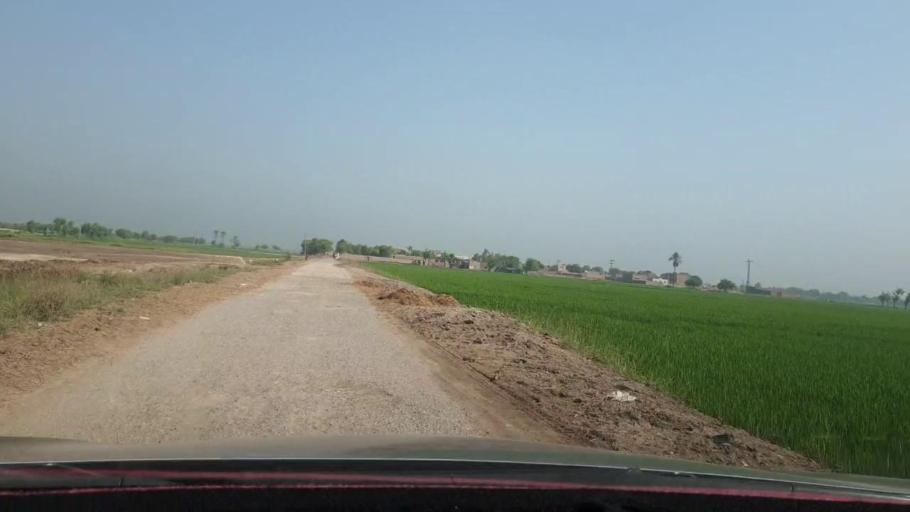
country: PK
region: Sindh
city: Kambar
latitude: 27.5990
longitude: 67.9365
